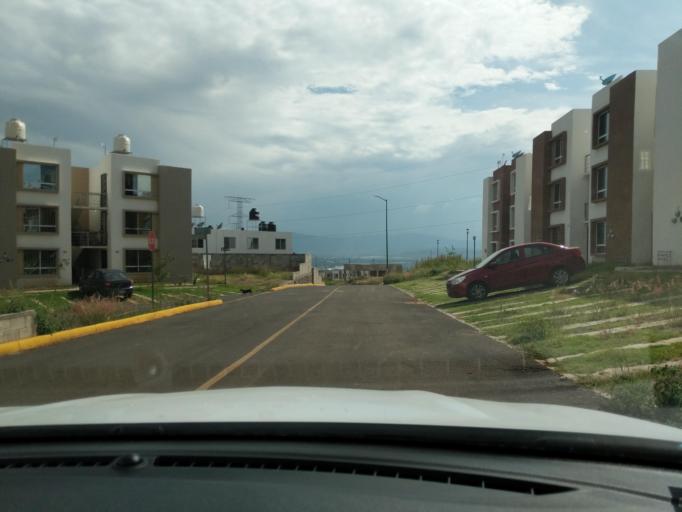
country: MX
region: Jalisco
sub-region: El Salto
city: El Muey
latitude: 20.5215
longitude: -103.2188
